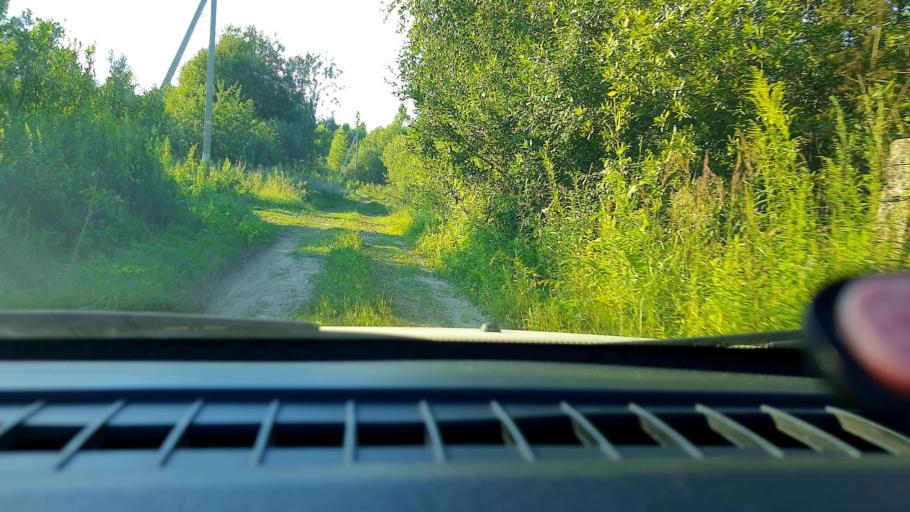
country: RU
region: Nizjnij Novgorod
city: Burevestnik
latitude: 56.0466
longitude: 43.8829
